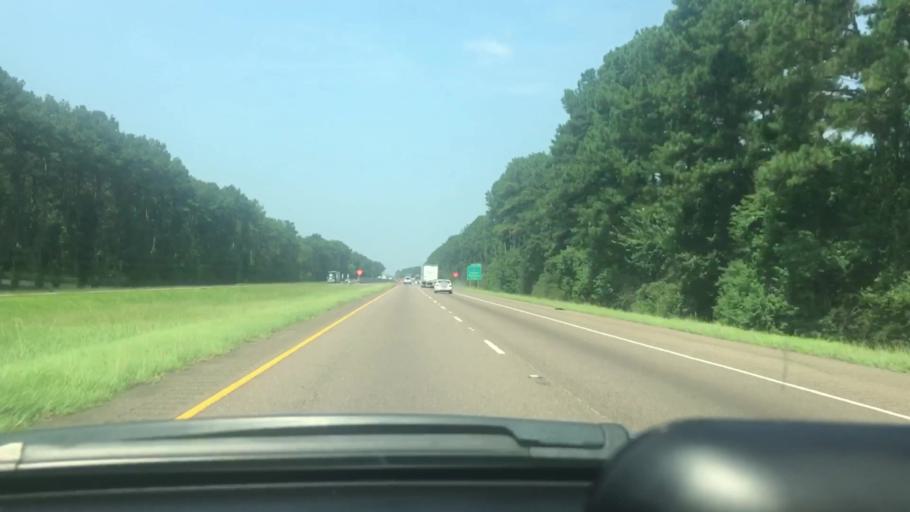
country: US
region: Louisiana
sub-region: Livingston Parish
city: Livingston
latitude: 30.4741
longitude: -90.7746
